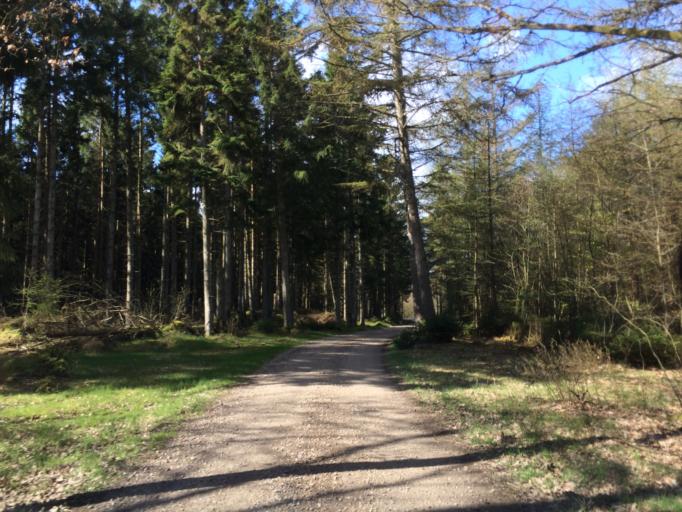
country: DK
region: Central Jutland
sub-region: Holstebro Kommune
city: Ulfborg
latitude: 56.2216
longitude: 8.4625
